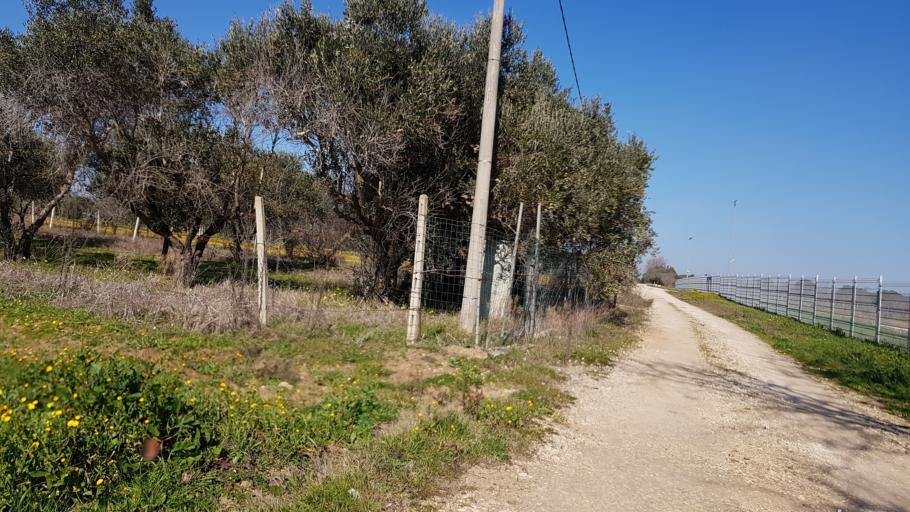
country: IT
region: Apulia
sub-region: Provincia di Brindisi
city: Mesagne
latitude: 40.6122
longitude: 17.8047
